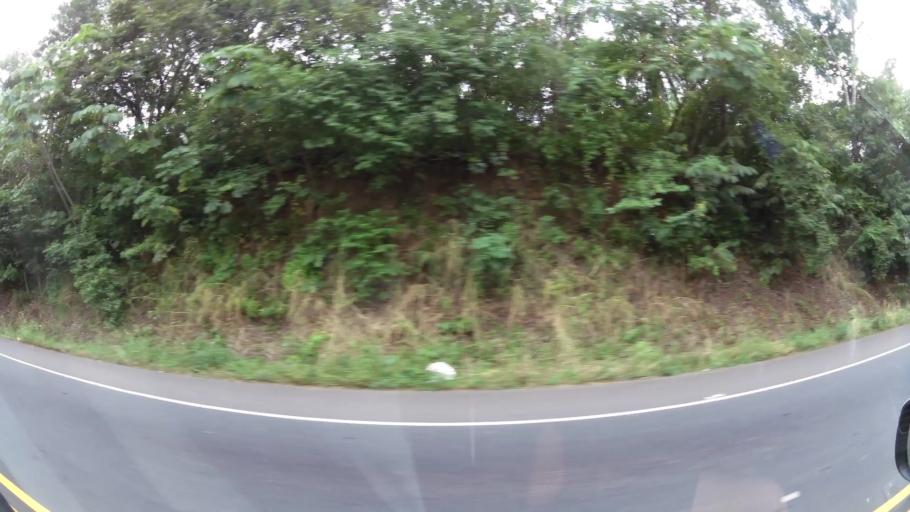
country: CR
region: Alajuela
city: Orotina
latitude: 9.8937
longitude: -84.6178
